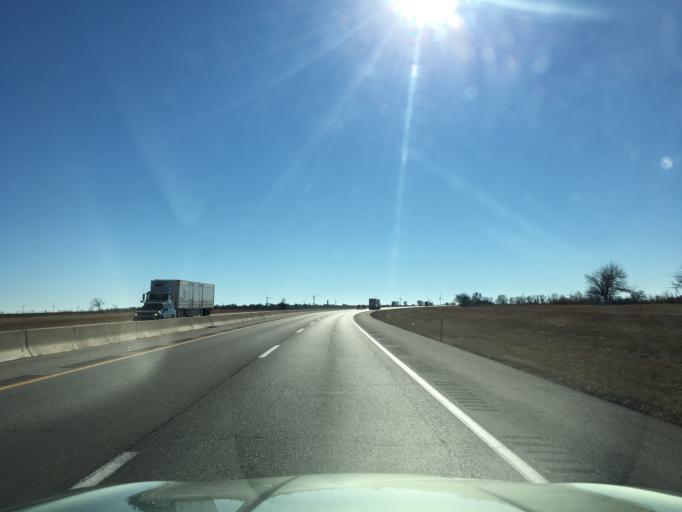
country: US
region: Kansas
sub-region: Sumner County
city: Wellington
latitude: 37.1857
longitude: -97.3404
